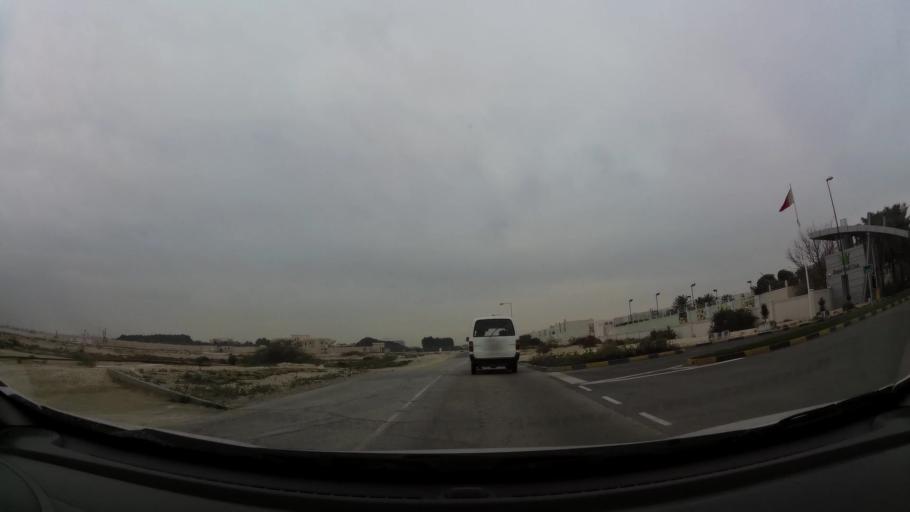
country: BH
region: Northern
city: Ar Rifa'
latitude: 26.0905
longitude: 50.5671
